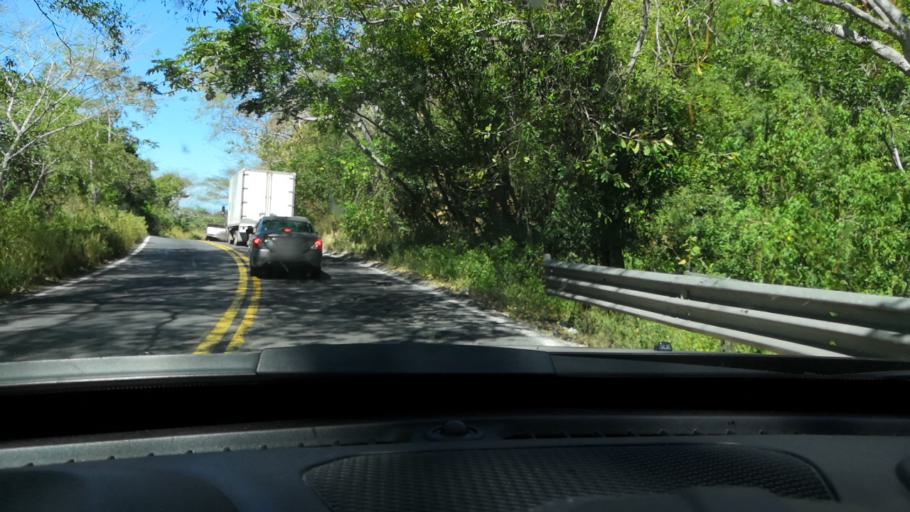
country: MX
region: Nayarit
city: Compostela
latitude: 21.2146
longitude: -104.9929
